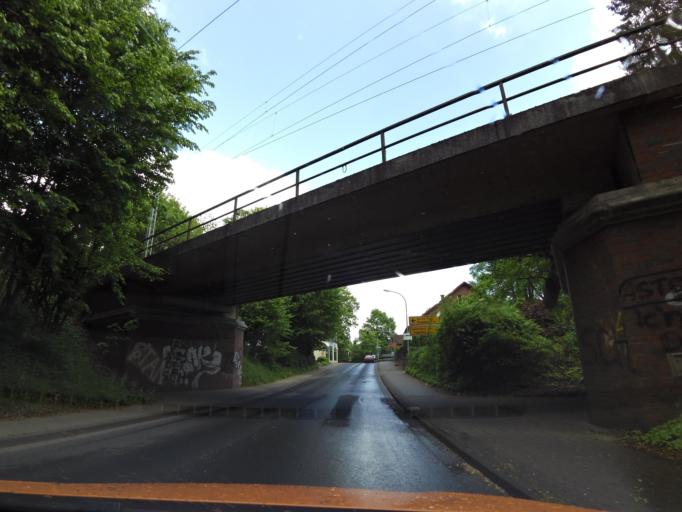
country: DE
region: Lower Saxony
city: Hude
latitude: 53.1153
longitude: 8.4525
